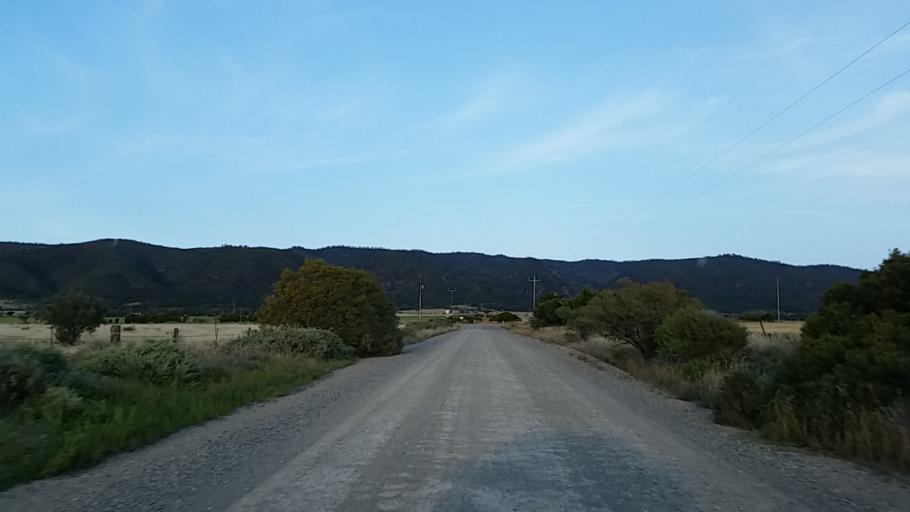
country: AU
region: South Australia
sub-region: Port Pirie City and Dists
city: Port Pirie
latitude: -33.0550
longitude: 138.0927
